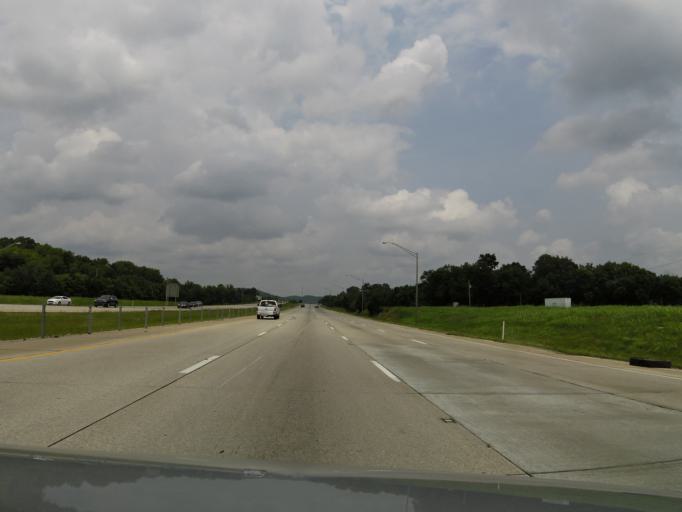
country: US
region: Kentucky
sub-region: Bullitt County
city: Shepherdsville
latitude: 37.9286
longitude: -85.6876
